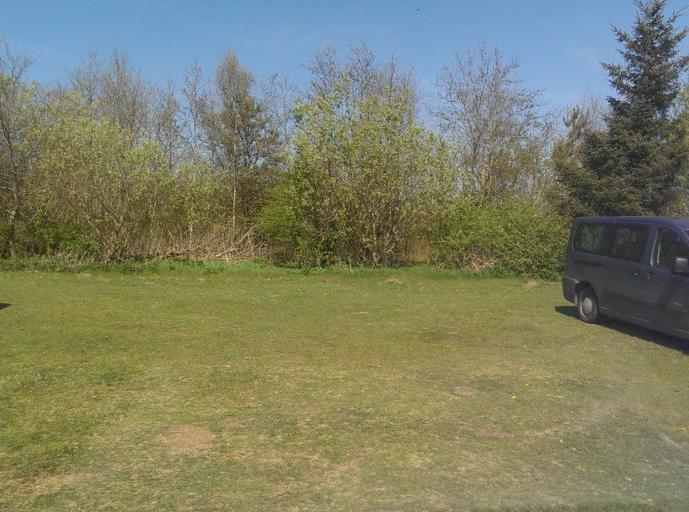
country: DK
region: South Denmark
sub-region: Esbjerg Kommune
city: Ribe
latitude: 55.3110
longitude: 8.7650
